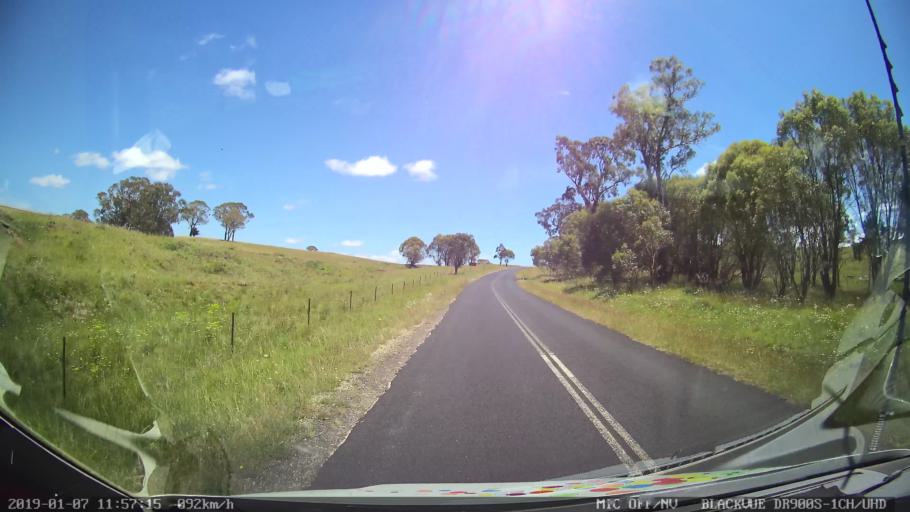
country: AU
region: New South Wales
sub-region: Guyra
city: Guyra
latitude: -30.2667
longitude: 151.6665
